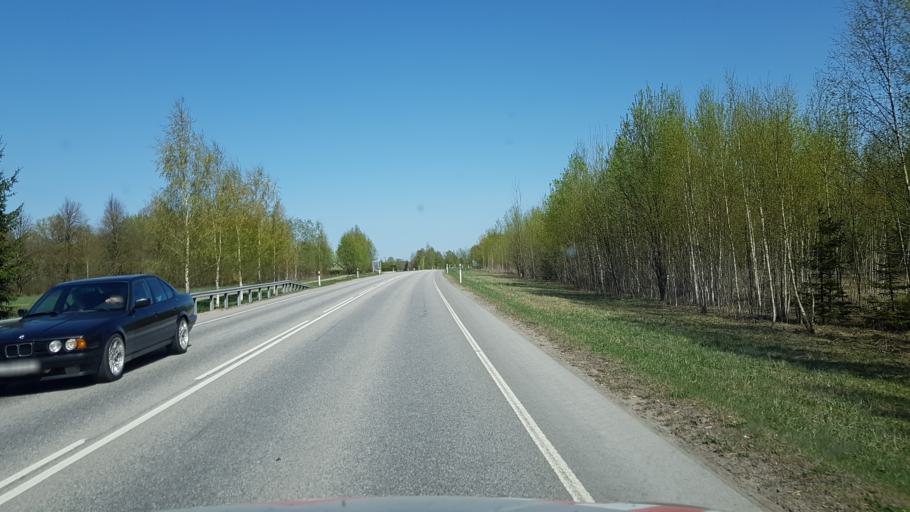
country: EE
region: Viljandimaa
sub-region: Viiratsi vald
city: Viiratsi
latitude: 58.3857
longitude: 25.6773
